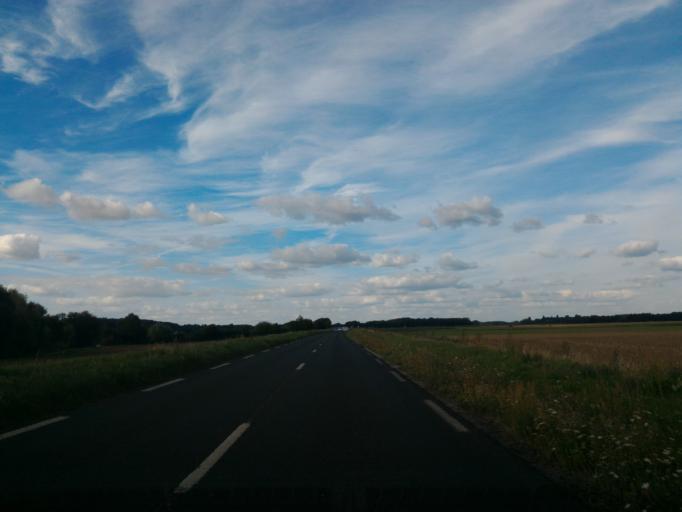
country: FR
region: Centre
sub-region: Departement du Loir-et-Cher
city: Saint-Claude-de-Diray
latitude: 47.6270
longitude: 1.4056
